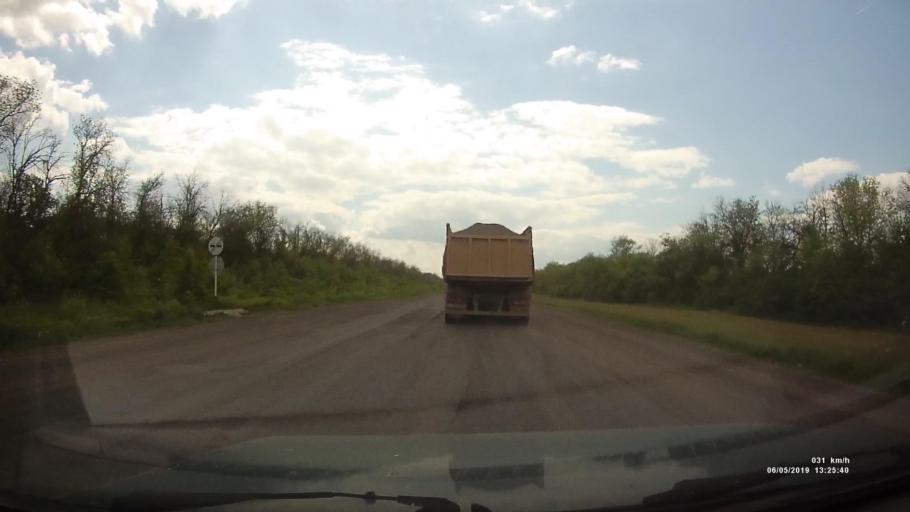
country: RU
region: Rostov
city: Ust'-Donetskiy
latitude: 47.6819
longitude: 40.9032
